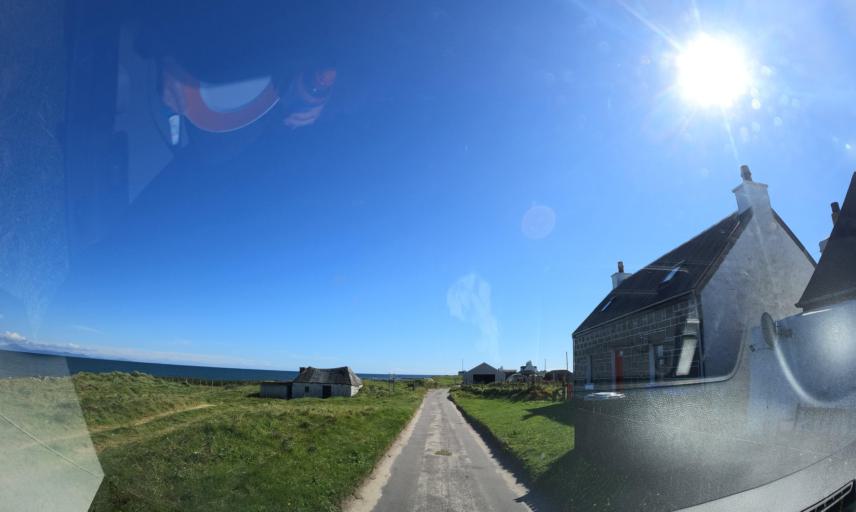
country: GB
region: Scotland
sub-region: Eilean Siar
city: Barra
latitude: 56.4647
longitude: -6.8953
